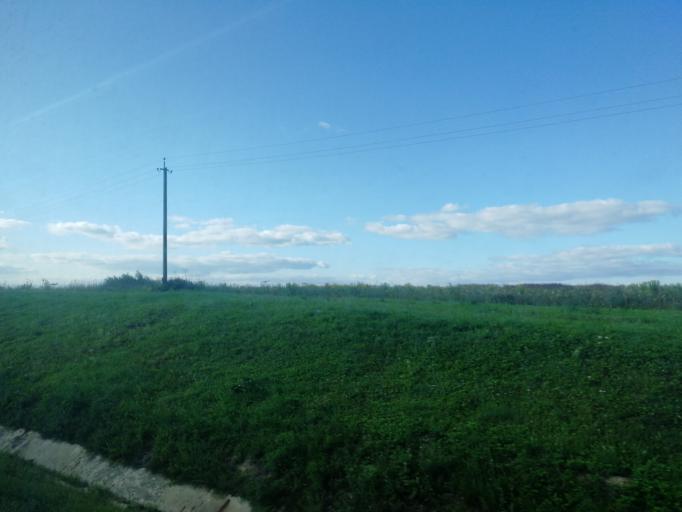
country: RU
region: Tula
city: Leninskiy
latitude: 54.2397
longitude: 37.3419
